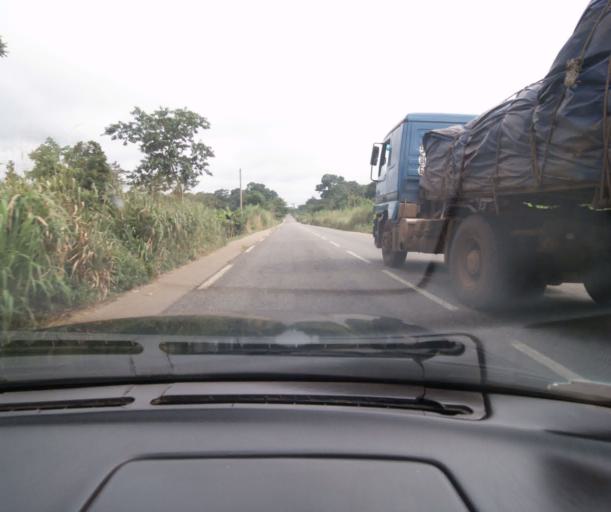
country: CM
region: Centre
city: Ombesa
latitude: 4.5919
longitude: 11.2622
